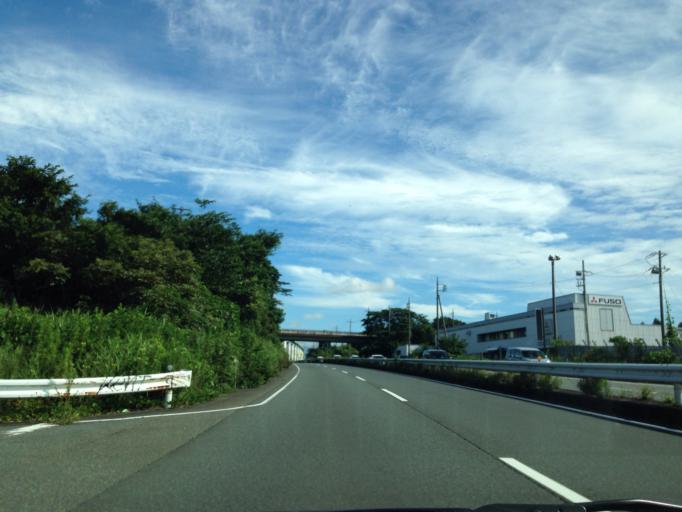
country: JP
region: Shizuoka
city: Gotemba
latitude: 35.2485
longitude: 138.9106
